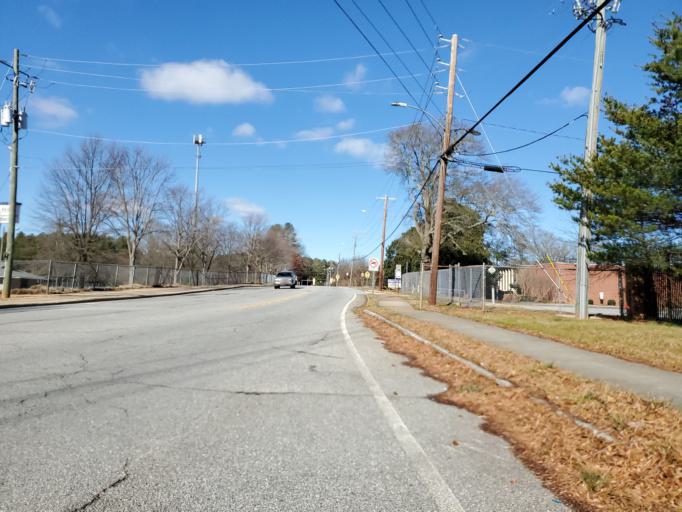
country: US
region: Georgia
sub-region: DeKalb County
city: Belvedere Park
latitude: 33.7584
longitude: -84.2689
